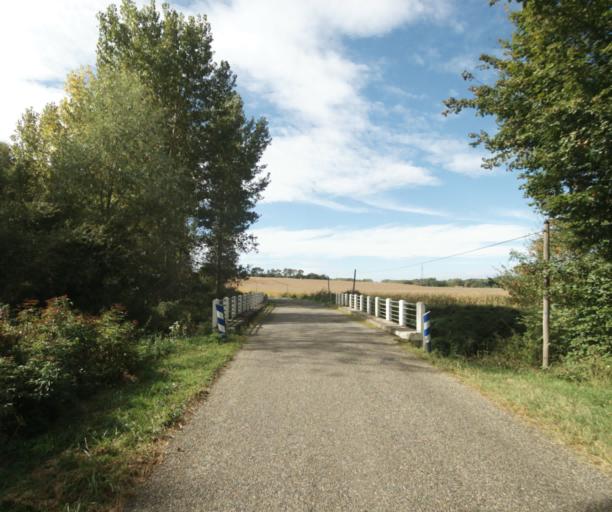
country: FR
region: Aquitaine
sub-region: Departement des Landes
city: Villeneuve-de-Marsan
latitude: 43.9012
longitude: -0.2213
